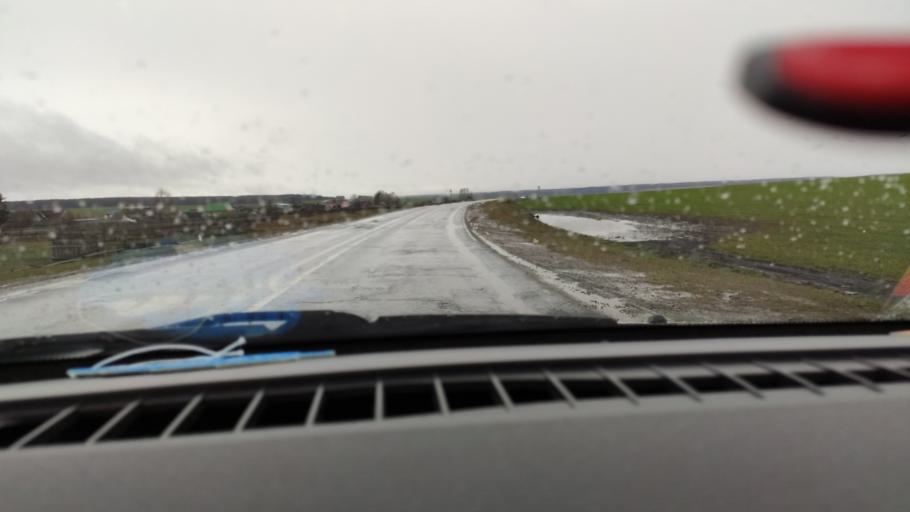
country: RU
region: Samara
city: Chelno-Vershiny
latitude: 54.6409
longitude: 50.9848
